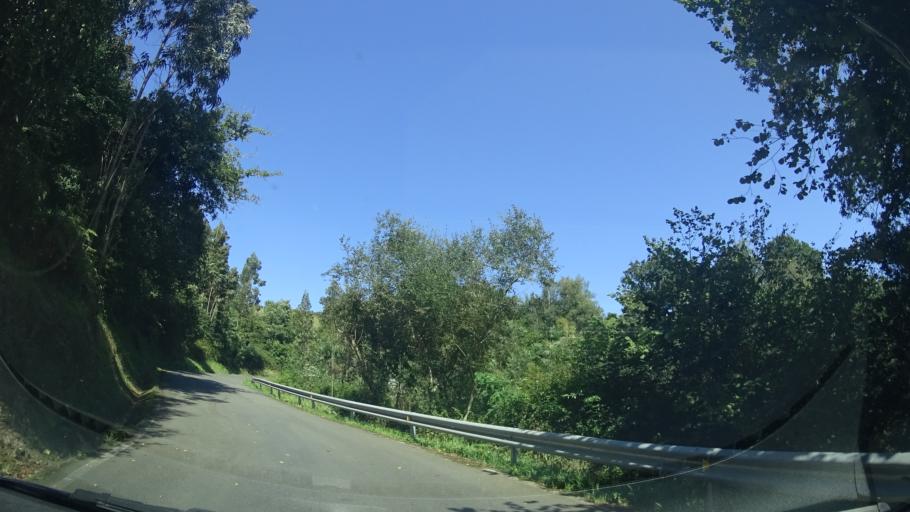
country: ES
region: Asturias
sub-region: Province of Asturias
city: Ribadesella
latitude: 43.4470
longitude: -5.0756
